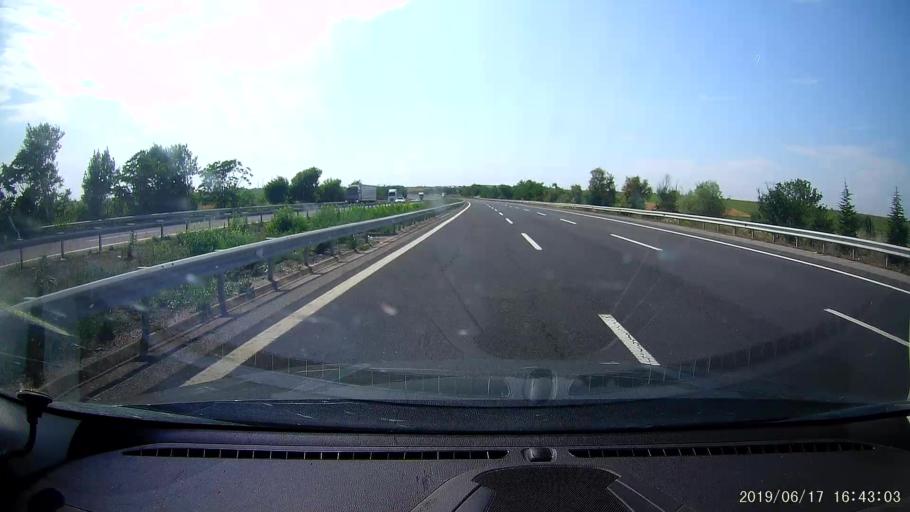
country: TR
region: Kirklareli
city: Luleburgaz
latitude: 41.4782
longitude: 27.3049
